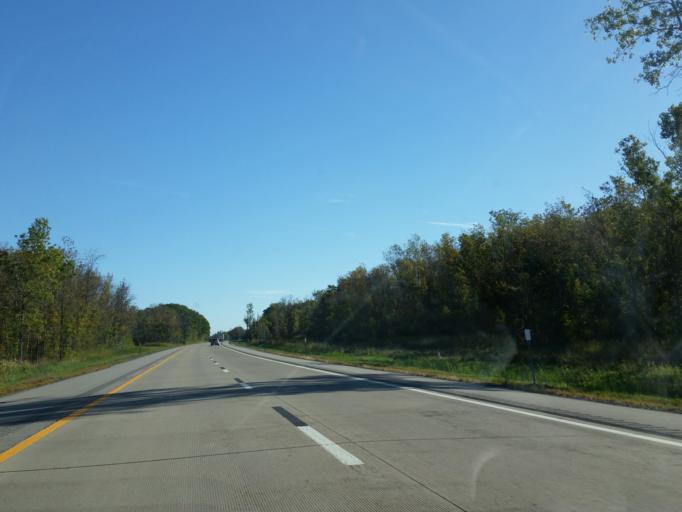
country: US
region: New York
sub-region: Erie County
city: Wanakah
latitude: 42.7134
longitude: -78.9027
